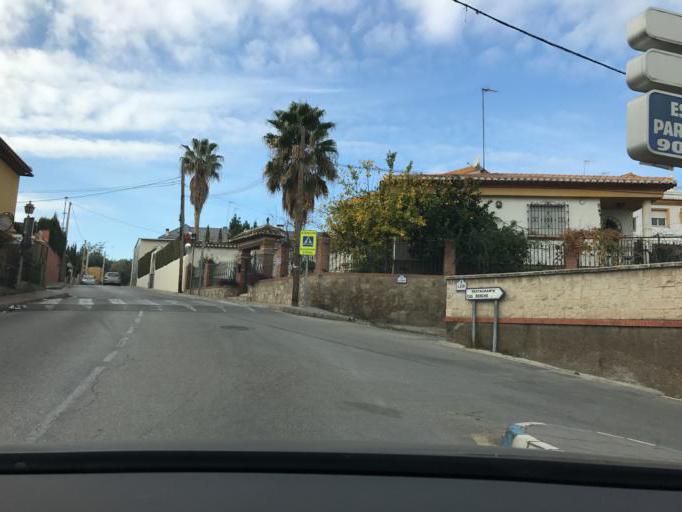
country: ES
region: Andalusia
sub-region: Provincia de Granada
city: Ogijares
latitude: 37.1144
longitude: -3.6143
